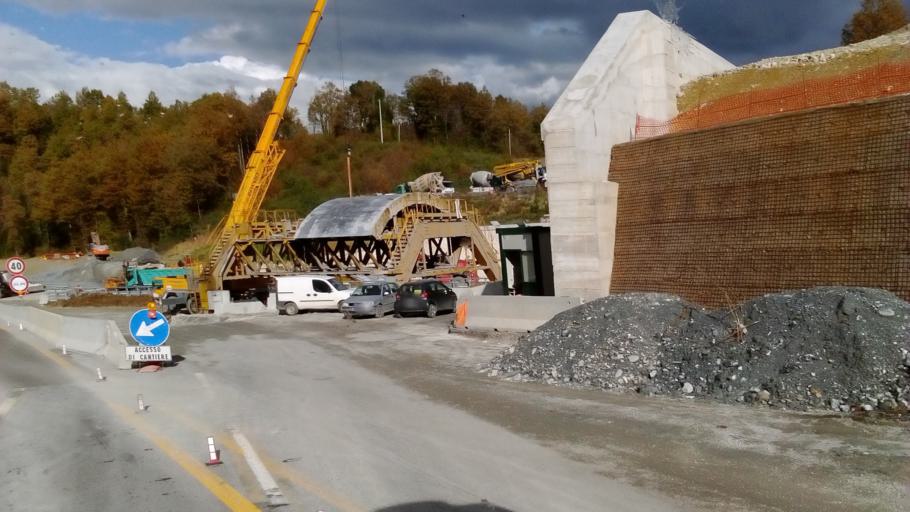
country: IT
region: Calabria
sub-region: Provincia di Cosenza
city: Laino Castello-Nuovo Centro
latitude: 39.9298
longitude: 15.9636
